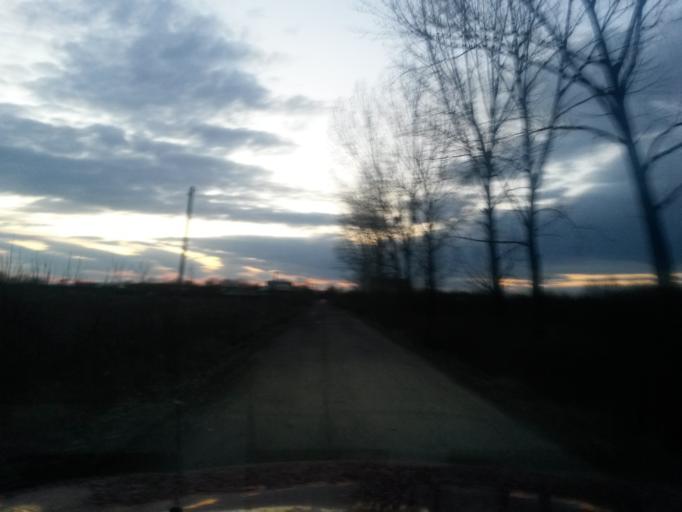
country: SK
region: Kosicky
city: Vinne
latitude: 48.6951
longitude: 22.0461
